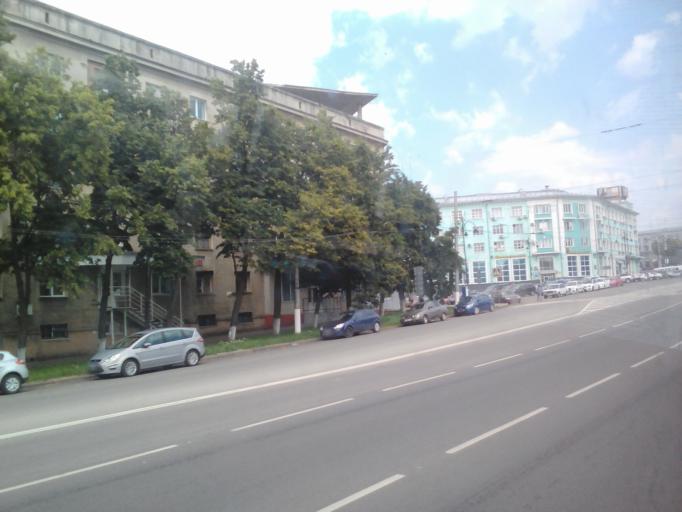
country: RU
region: Kursk
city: Kursk
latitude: 51.7287
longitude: 36.1926
